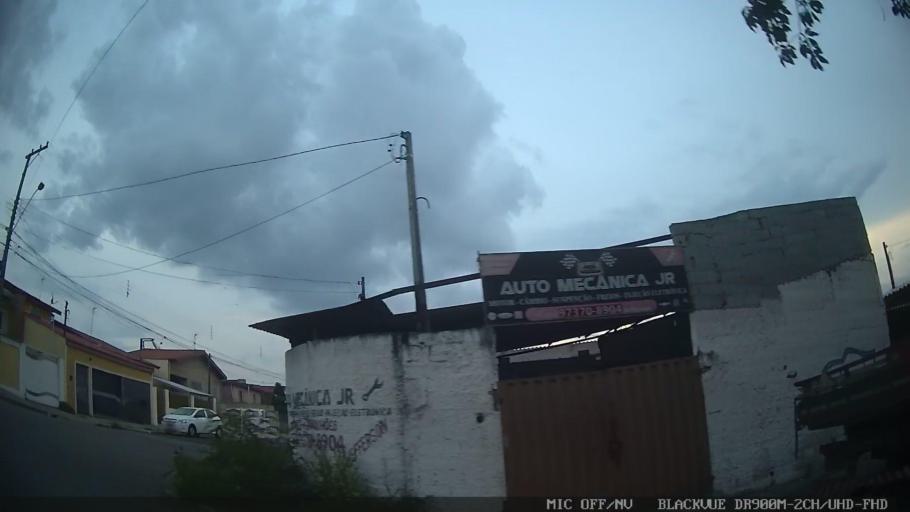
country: BR
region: Sao Paulo
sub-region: Atibaia
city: Atibaia
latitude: -23.1282
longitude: -46.5708
